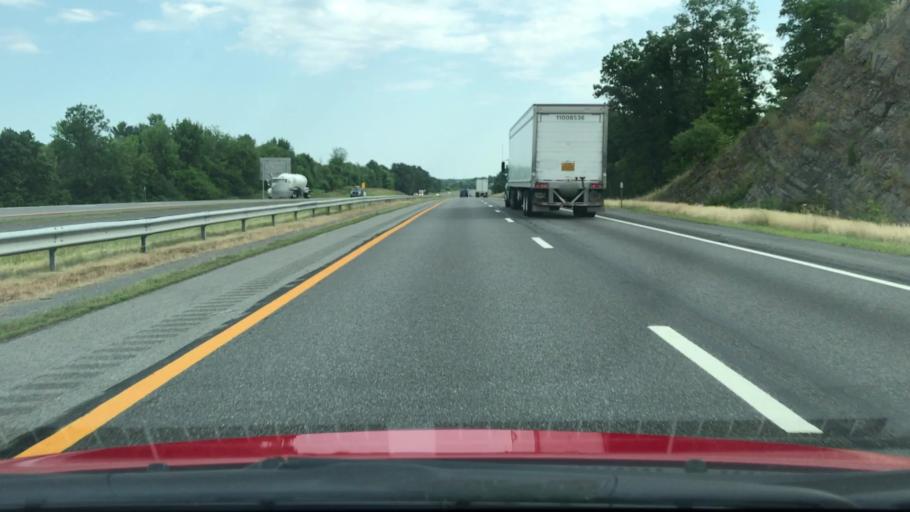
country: US
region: New York
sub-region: Albany County
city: Ravena
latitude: 42.4548
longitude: -73.8104
